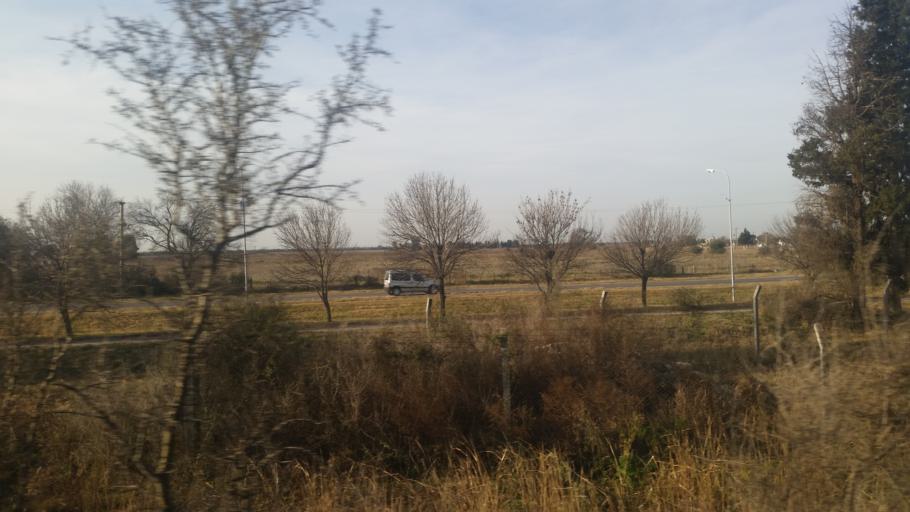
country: AR
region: Cordoba
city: Toledo
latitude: -31.5505
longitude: -64.0152
